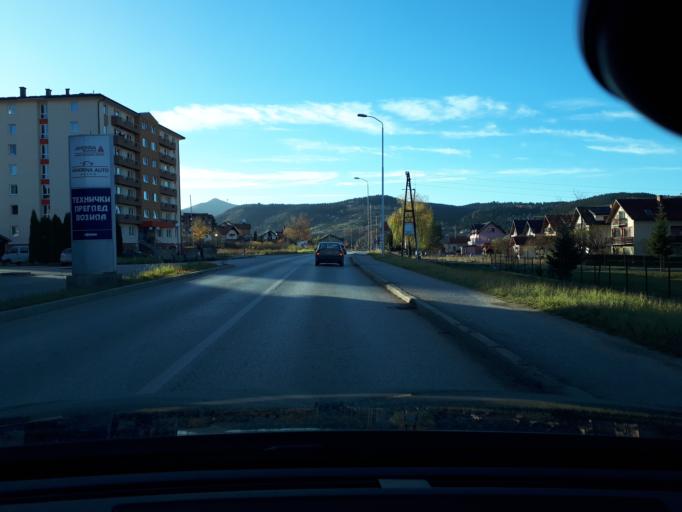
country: BA
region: Republika Srpska
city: Koran
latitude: 43.8123
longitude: 18.5688
